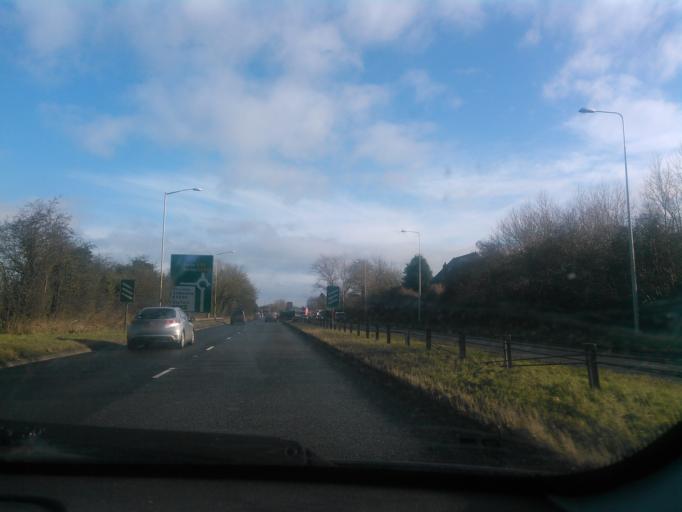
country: GB
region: England
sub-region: Staffordshire
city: Uttoxeter
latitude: 52.9096
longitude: -1.8779
